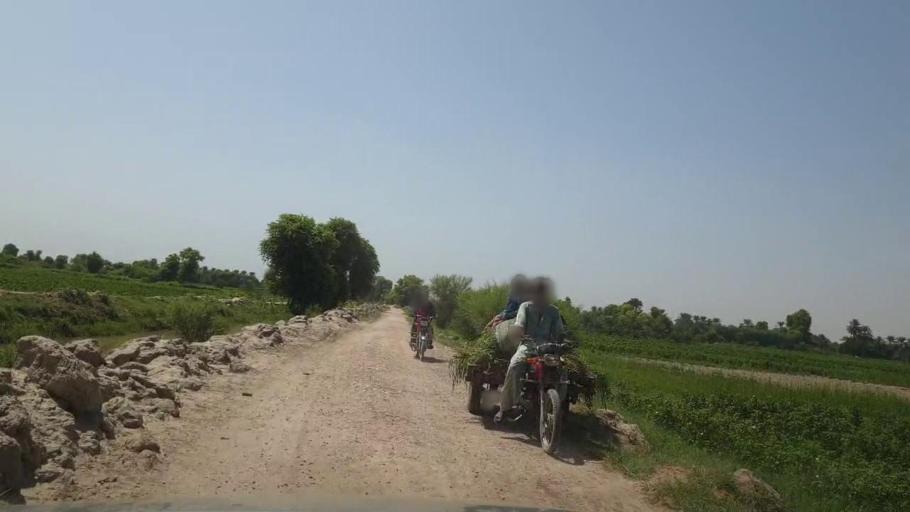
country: PK
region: Sindh
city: Rohri
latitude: 27.6509
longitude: 68.9838
